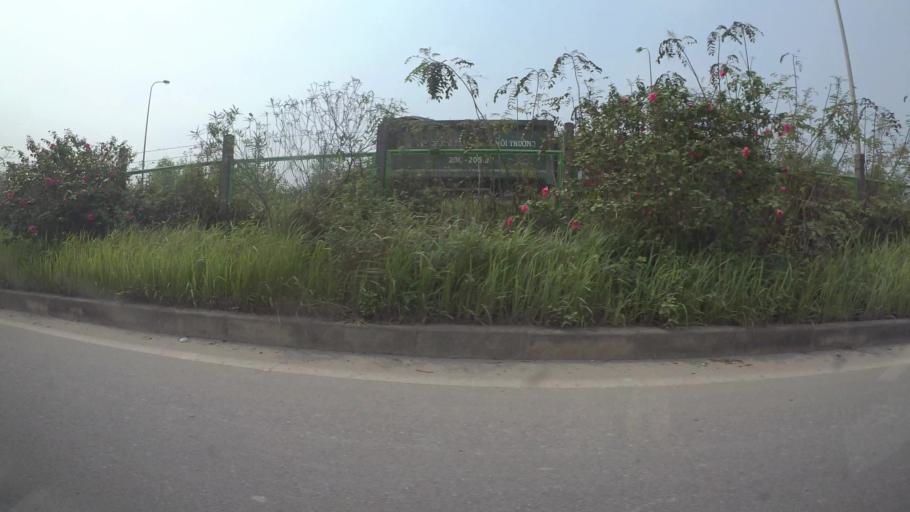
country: VN
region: Ha Noi
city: Quoc Oai
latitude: 21.0020
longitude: 105.6181
